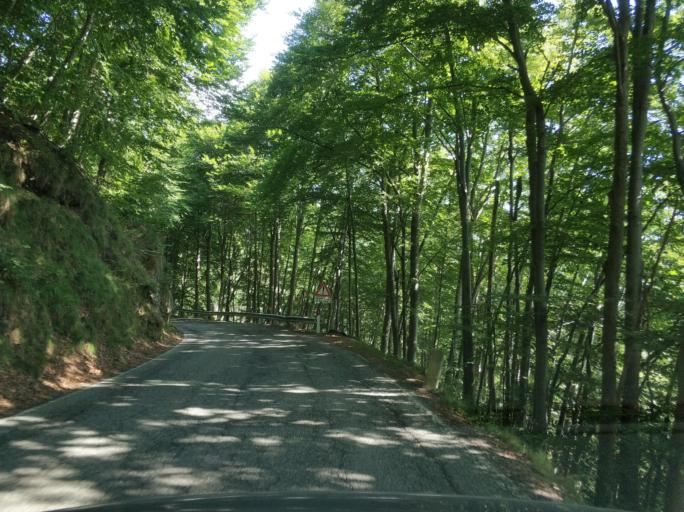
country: IT
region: Piedmont
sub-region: Provincia di Torino
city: Viu
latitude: 45.1887
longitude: 7.3655
